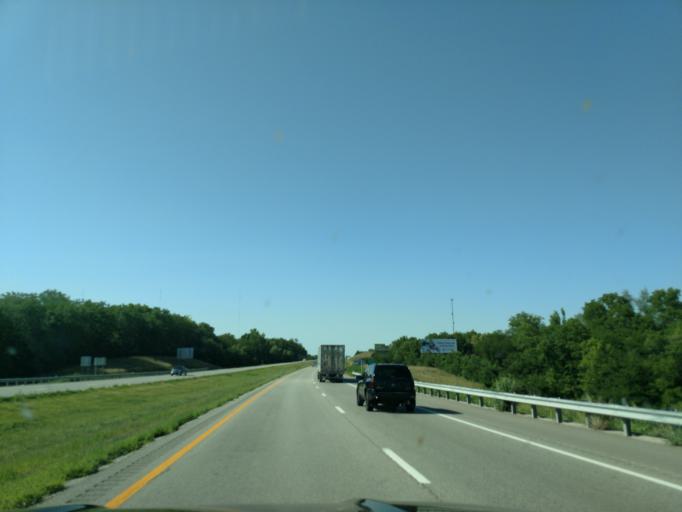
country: US
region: Missouri
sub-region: Andrew County
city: Country Club Village
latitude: 39.8204
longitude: -94.8051
